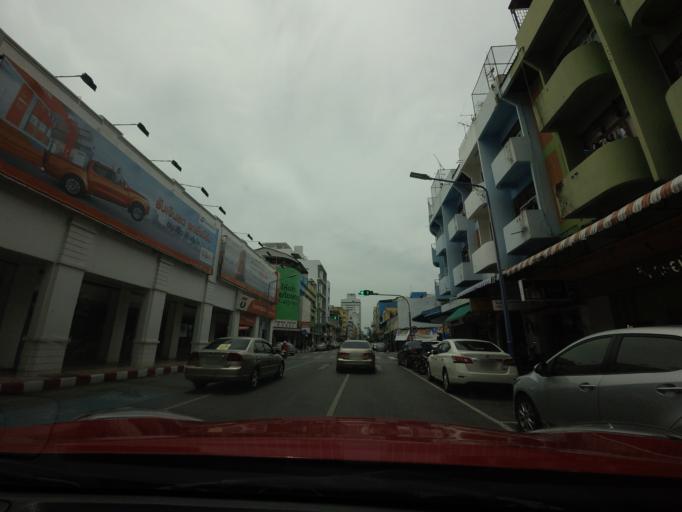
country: TH
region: Songkhla
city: Hat Yai
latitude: 7.0025
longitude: 100.4704
